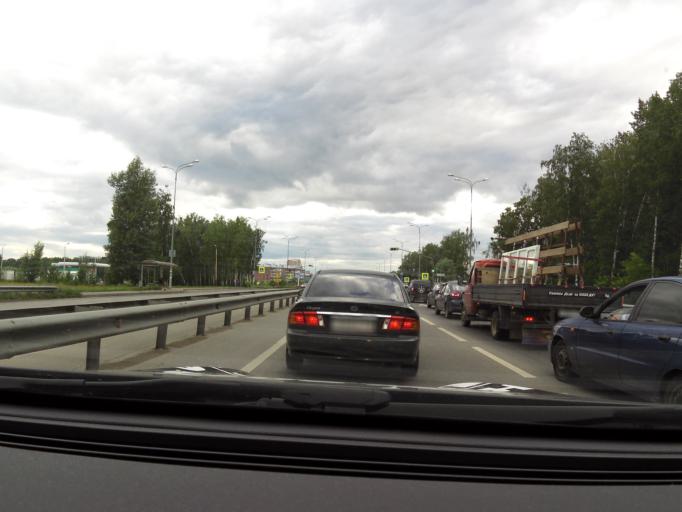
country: RU
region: Tatarstan
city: Osinovo
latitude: 55.8468
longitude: 48.9186
